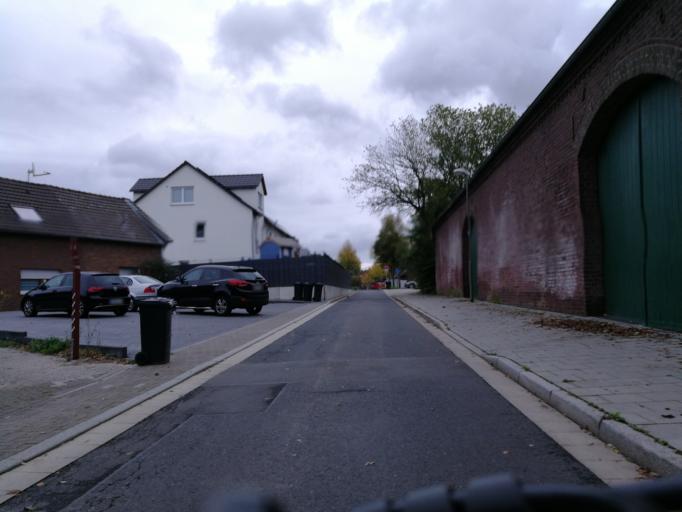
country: DE
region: North Rhine-Westphalia
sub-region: Regierungsbezirk Dusseldorf
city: Neuss
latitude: 51.1344
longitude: 6.7376
